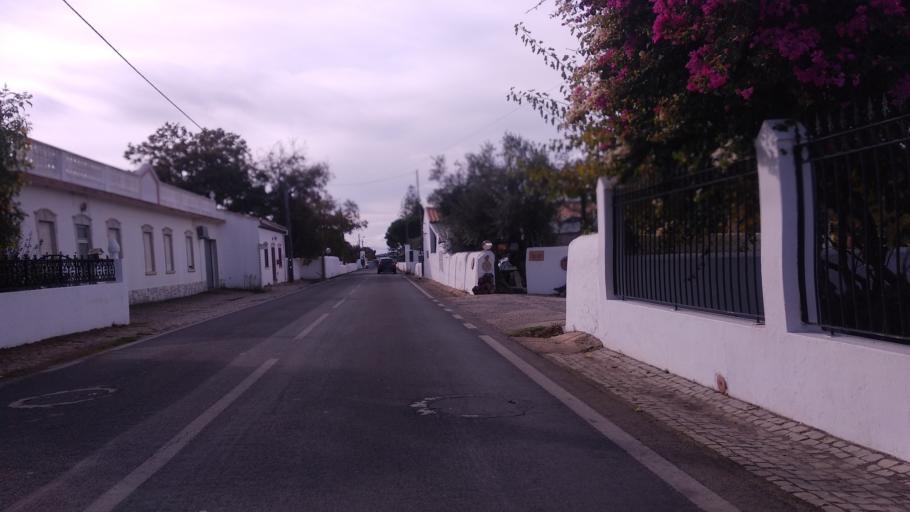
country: PT
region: Faro
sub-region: Sao Bras de Alportel
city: Sao Bras de Alportel
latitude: 37.1525
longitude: -7.9125
